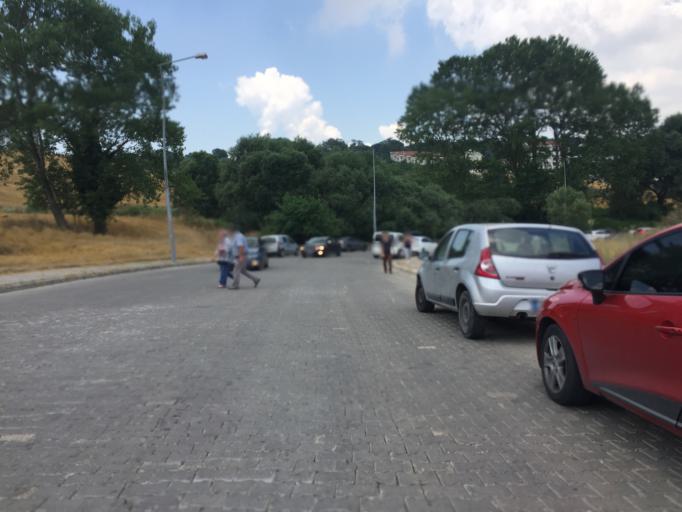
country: TR
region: Istanbul
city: Esenyurt
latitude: 41.0789
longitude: 28.6631
